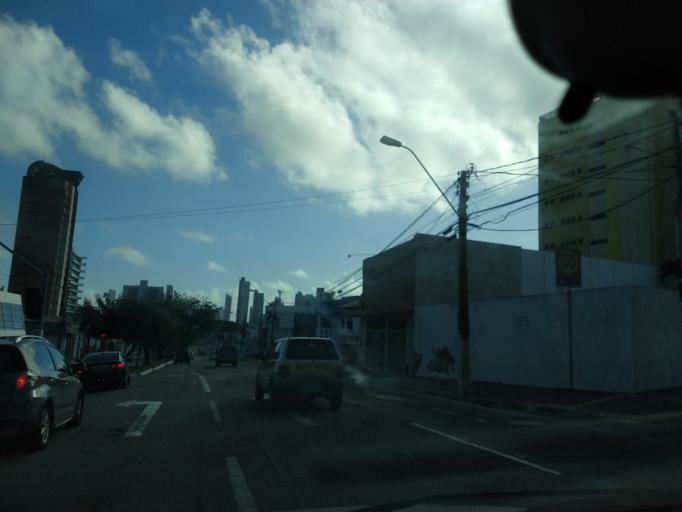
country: BR
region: Rio Grande do Norte
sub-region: Natal
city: Natal
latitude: -5.7996
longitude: -35.2001
